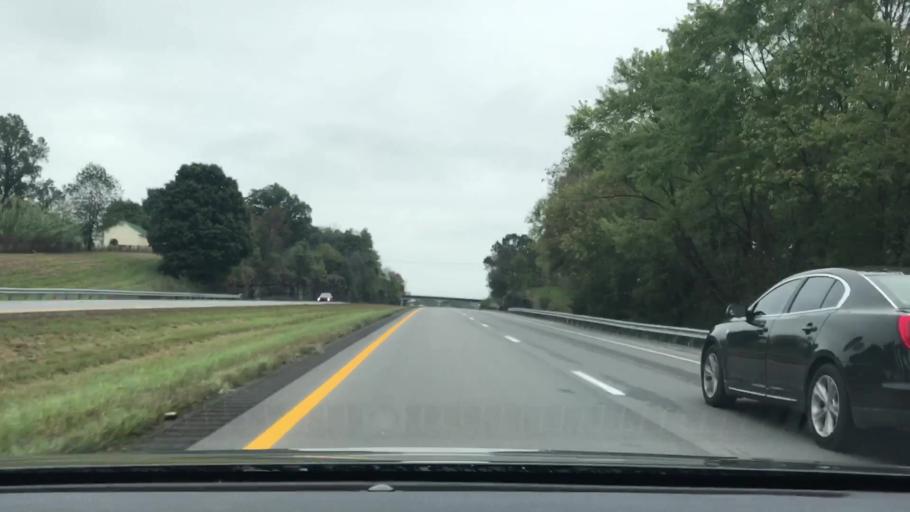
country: US
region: Kentucky
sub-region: Adair County
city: Columbia
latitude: 37.0880
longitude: -85.2705
